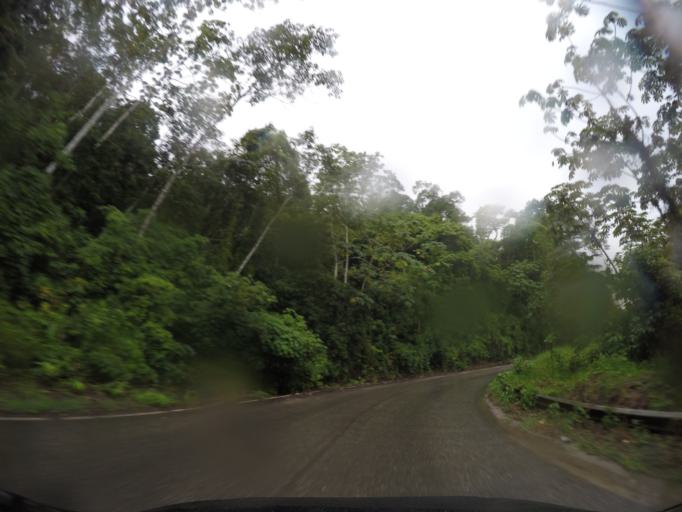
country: MX
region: Oaxaca
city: San Gabriel Mixtepec
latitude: 16.0804
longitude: -97.0832
